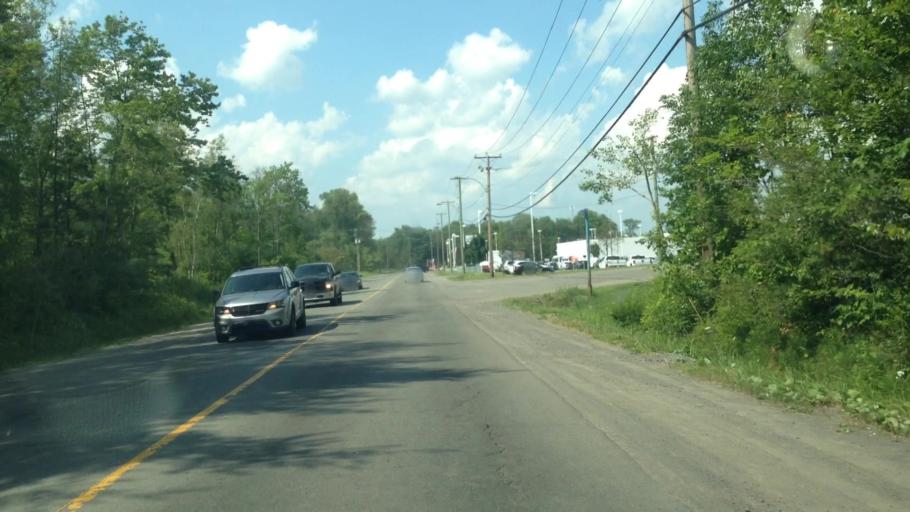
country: CA
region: Quebec
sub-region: Laurentides
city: Saint-Jerome
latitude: 45.7718
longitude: -74.0228
